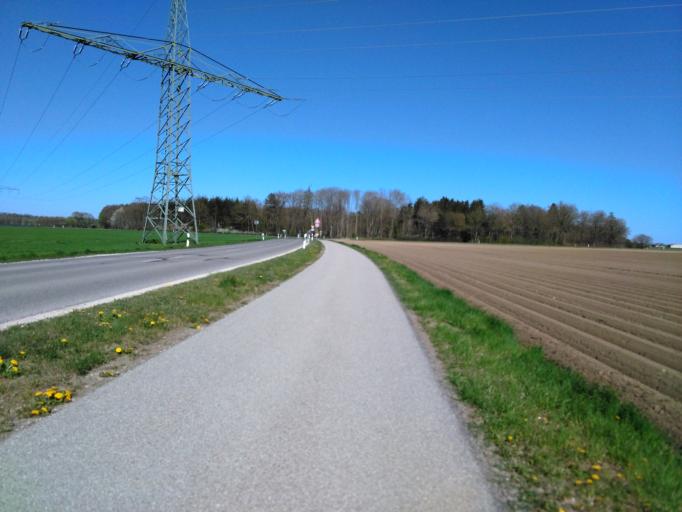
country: DE
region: Bavaria
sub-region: Upper Bavaria
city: Mammendorf
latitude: 48.2110
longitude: 11.1882
